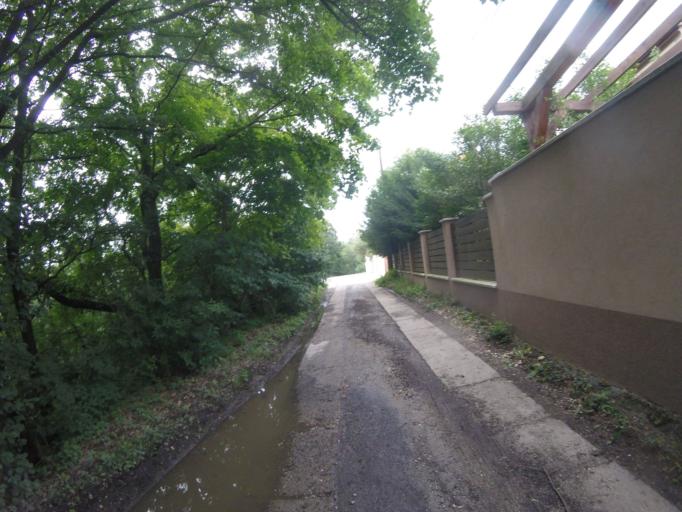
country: HU
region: Pest
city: Toeroekbalint
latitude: 47.4304
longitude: 18.9254
